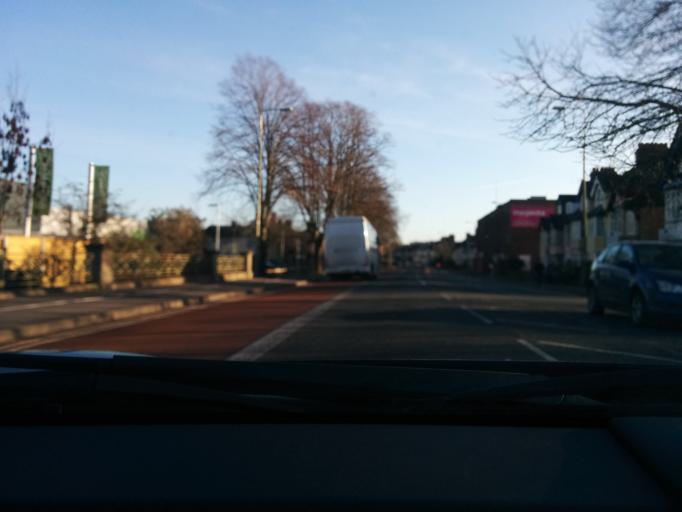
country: GB
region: England
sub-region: Oxfordshire
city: Oxford
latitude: 51.7526
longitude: -1.2814
